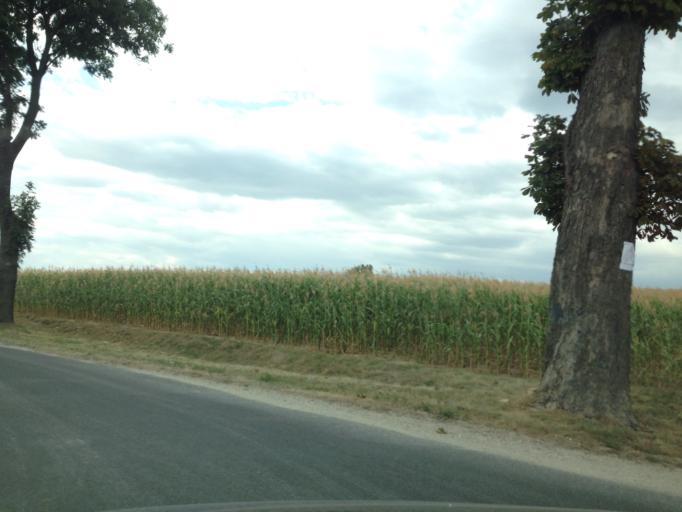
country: PL
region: Kujawsko-Pomorskie
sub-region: Powiat golubsko-dobrzynski
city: Kowalewo Pomorskie
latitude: 53.1822
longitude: 18.8399
